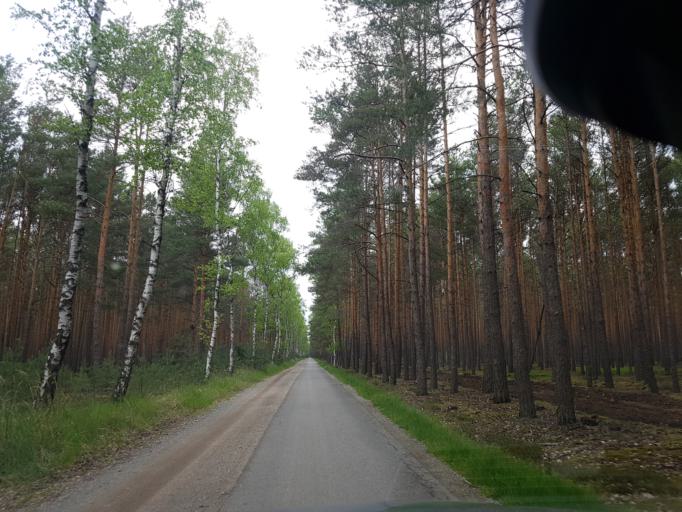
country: DE
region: Brandenburg
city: Crinitz
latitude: 51.6860
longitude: 13.7783
